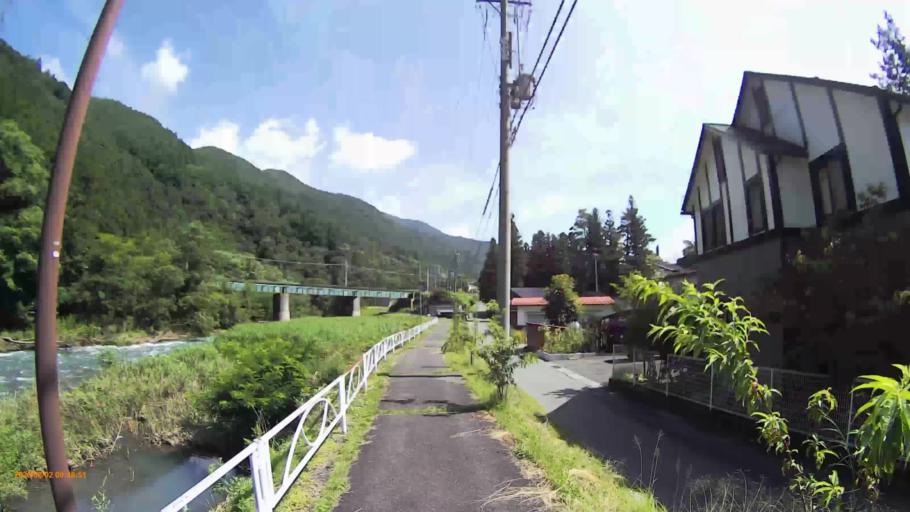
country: JP
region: Nagano
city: Tatsuno
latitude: 35.9759
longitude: 137.8254
